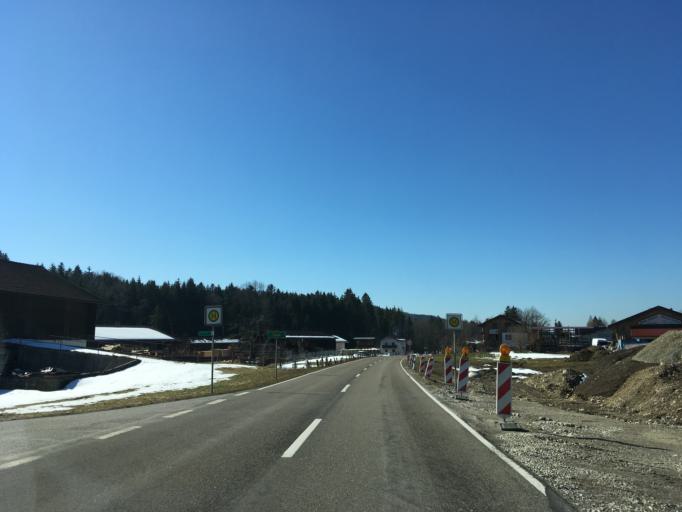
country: DE
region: Bavaria
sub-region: Upper Bavaria
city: Frasdorf
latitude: 47.7971
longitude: 12.2445
